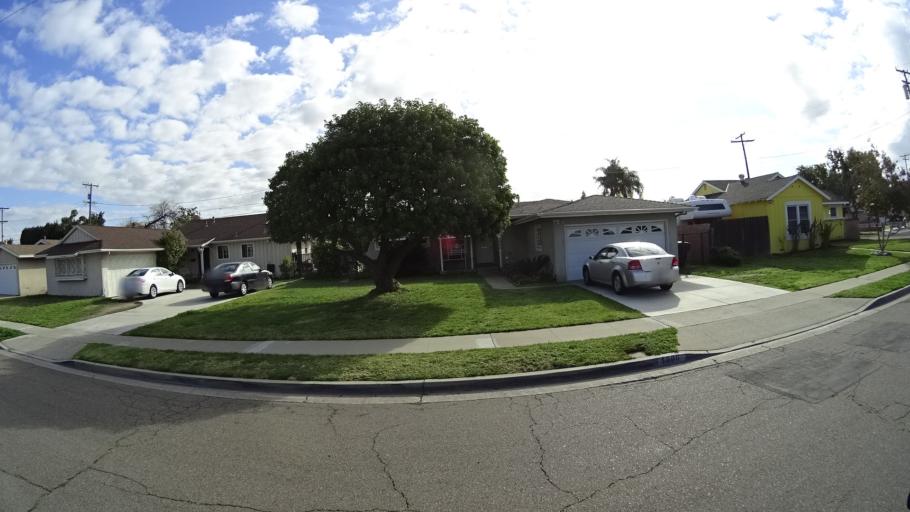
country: US
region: California
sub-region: Orange County
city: Anaheim
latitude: 33.8520
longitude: -117.9049
